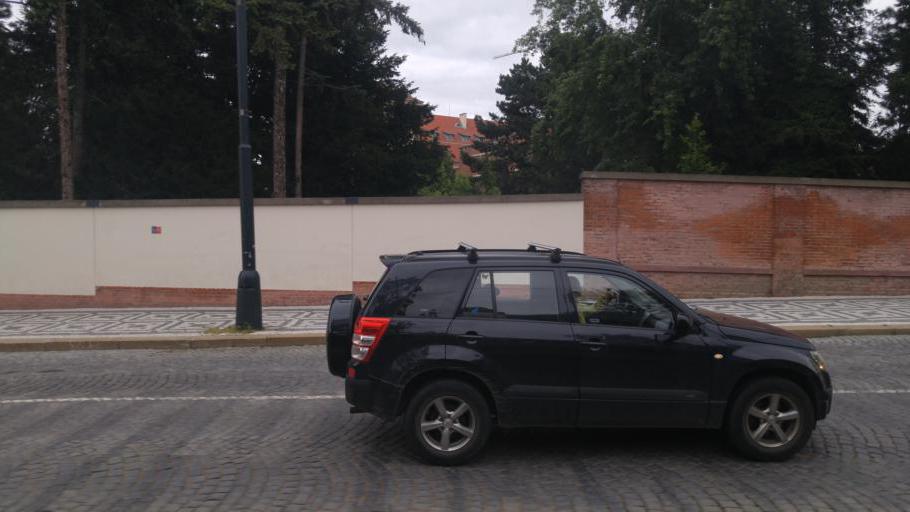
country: CZ
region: Praha
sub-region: Praha 1
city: Mala Strana
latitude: 50.0895
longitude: 14.3880
